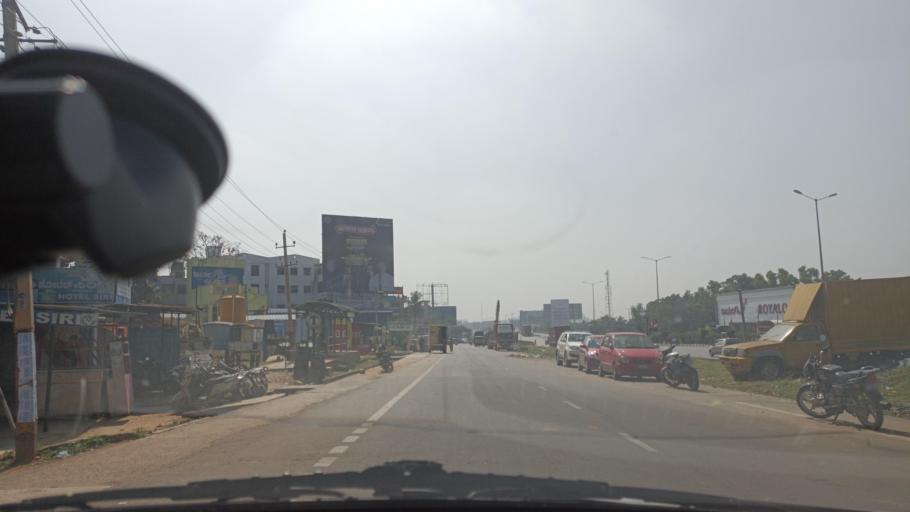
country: IN
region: Karnataka
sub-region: Bangalore Rural
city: Devanhalli
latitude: 13.1842
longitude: 77.6417
